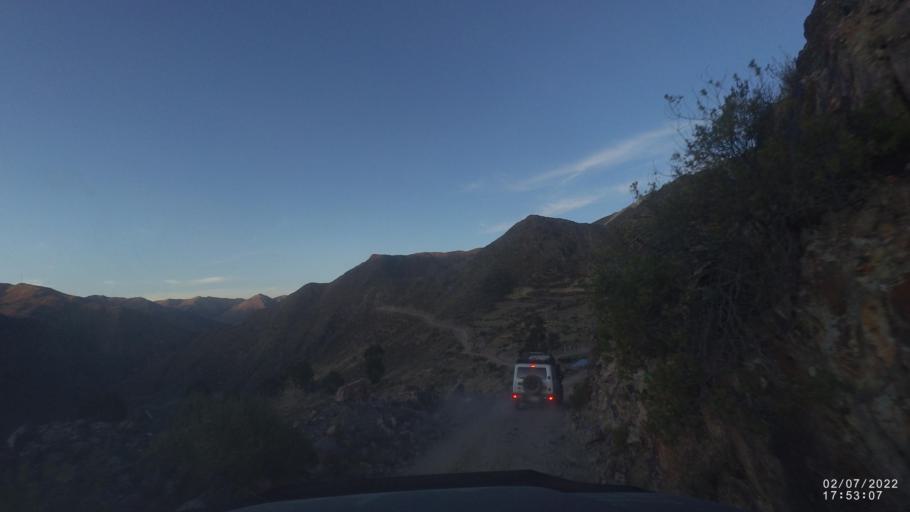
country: BO
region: Cochabamba
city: Irpa Irpa
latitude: -17.8447
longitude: -66.6180
